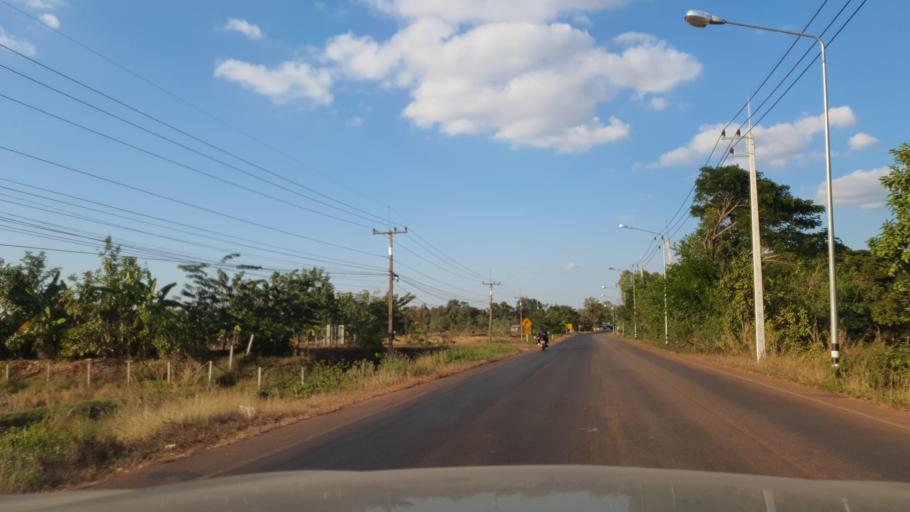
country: TH
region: Sakon Nakhon
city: Phon Na Kaeo
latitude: 17.2674
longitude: 104.1916
